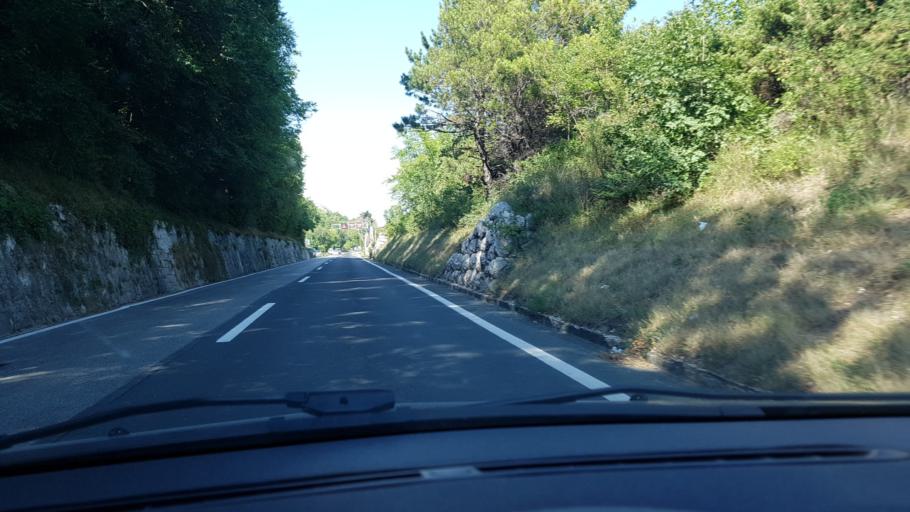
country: HR
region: Splitsko-Dalmatinska
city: Klis
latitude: 43.5651
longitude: 16.5281
